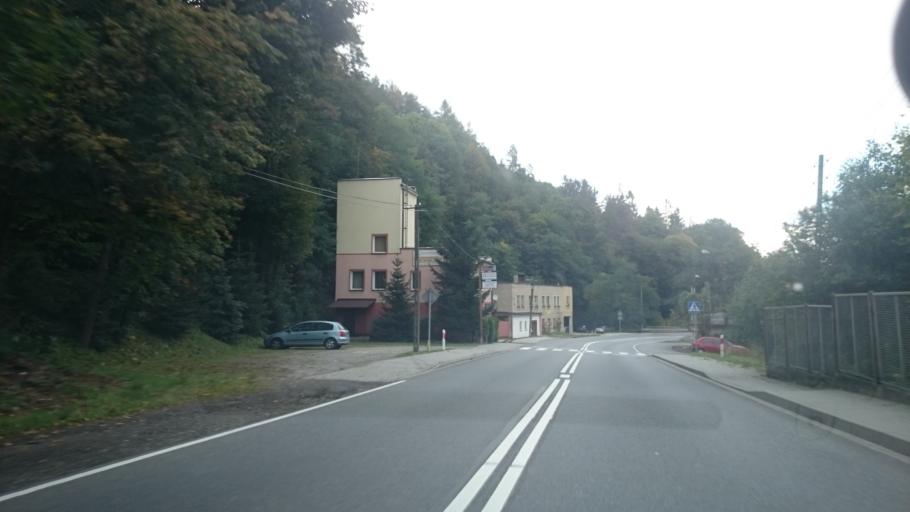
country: PL
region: Lower Silesian Voivodeship
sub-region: Powiat zabkowicki
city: Zloty Stok
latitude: 50.4427
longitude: 16.8319
